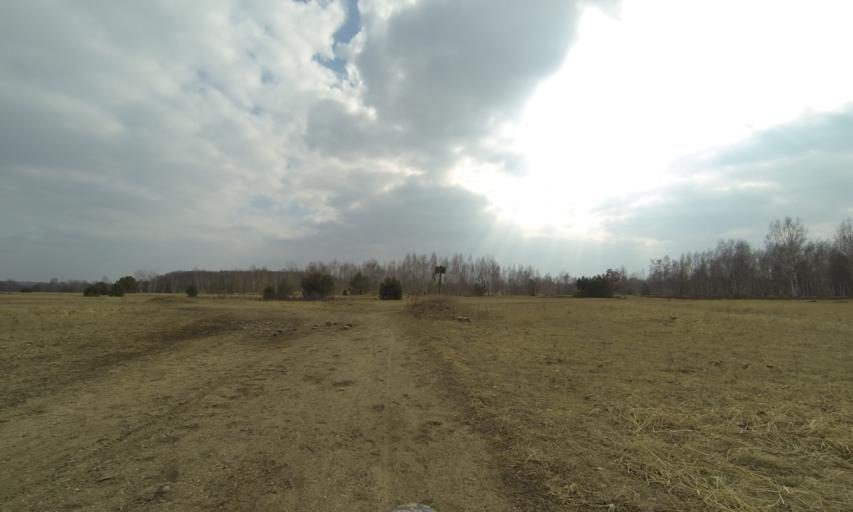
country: DE
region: Saxony
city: Albertstadt
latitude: 51.0989
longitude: 13.7443
